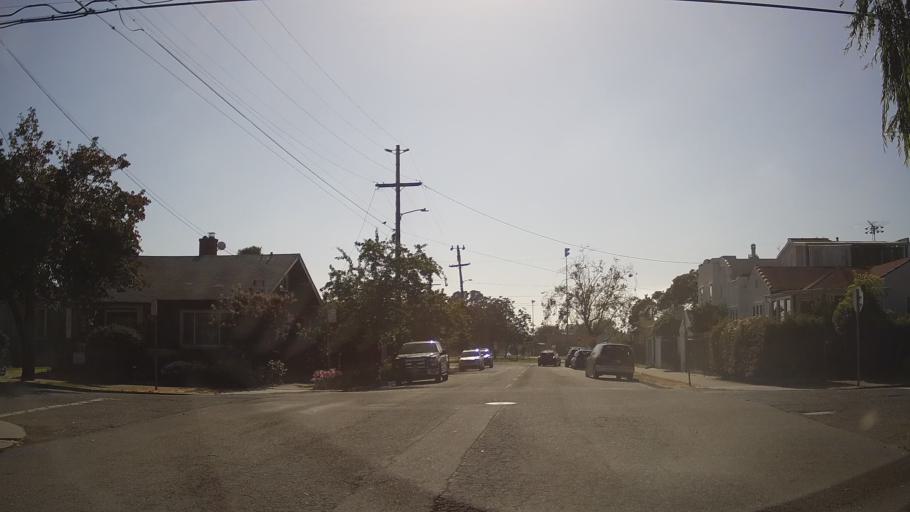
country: US
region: California
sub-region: Alameda County
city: Berkeley
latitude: 37.8558
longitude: -122.2820
